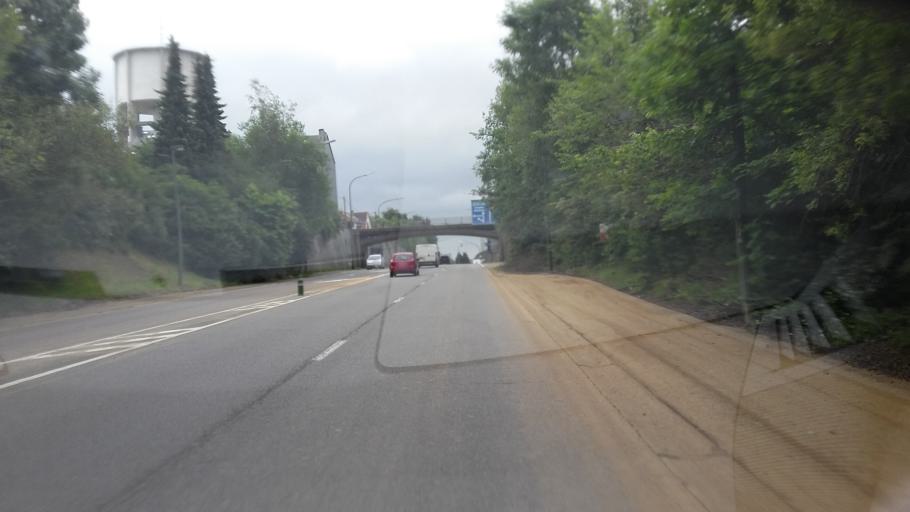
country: BE
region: Wallonia
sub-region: Province du Luxembourg
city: Arlon
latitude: 49.6879
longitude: 5.8201
